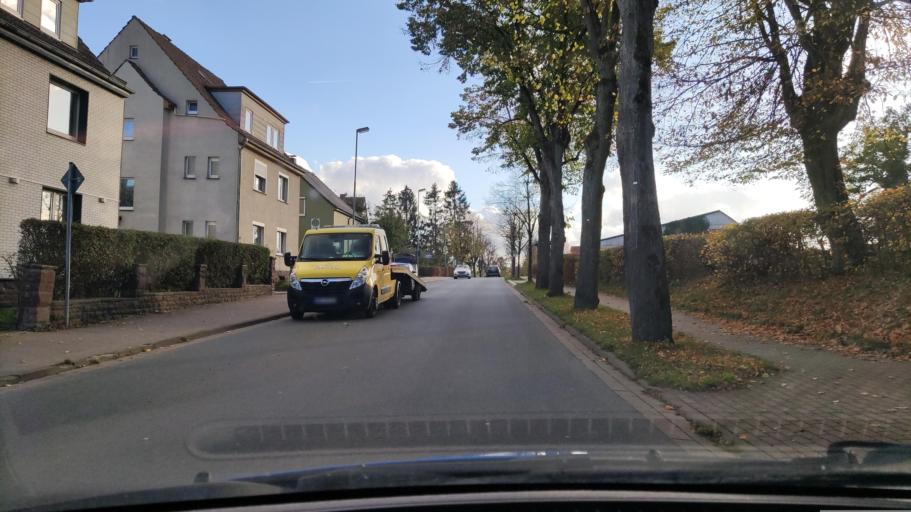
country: DE
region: Lower Saxony
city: Stadtoldendorf
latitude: 51.8792
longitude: 9.6226
